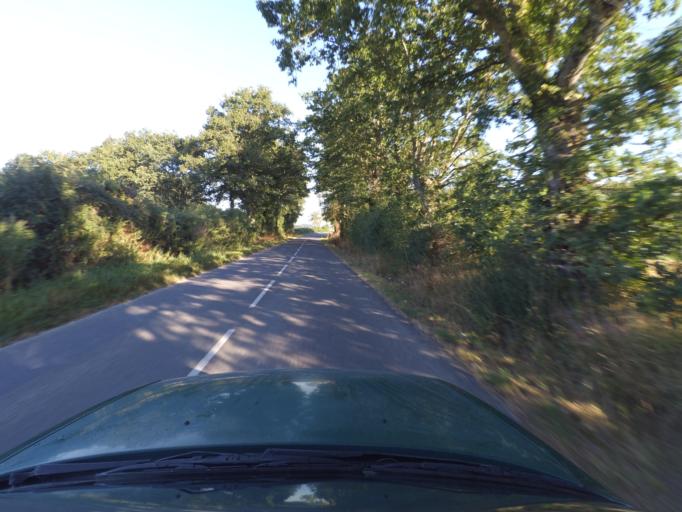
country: FR
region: Pays de la Loire
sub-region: Departement de la Loire-Atlantique
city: La Planche
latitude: 47.0241
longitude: -1.4627
